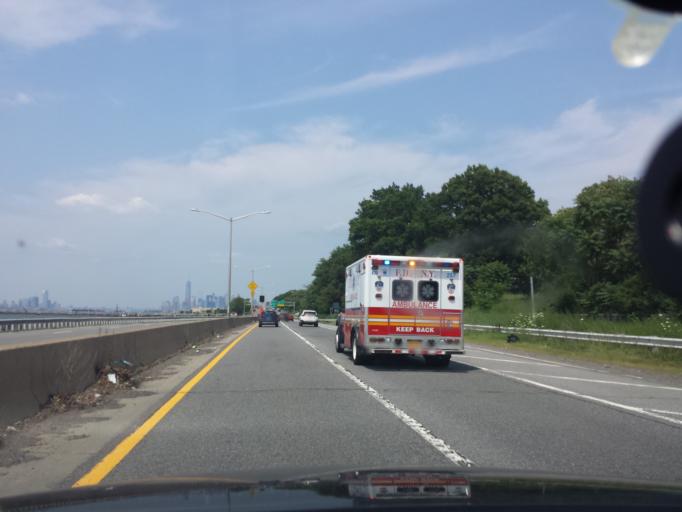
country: US
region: New York
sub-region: Kings County
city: Bensonhurst
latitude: 40.6346
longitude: -74.0386
